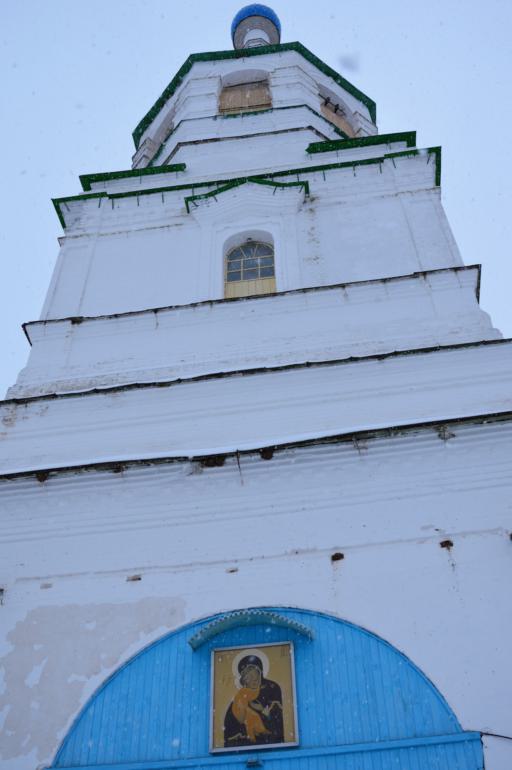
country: RU
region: Kirov
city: Darovskoy
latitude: 58.9149
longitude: 48.0074
